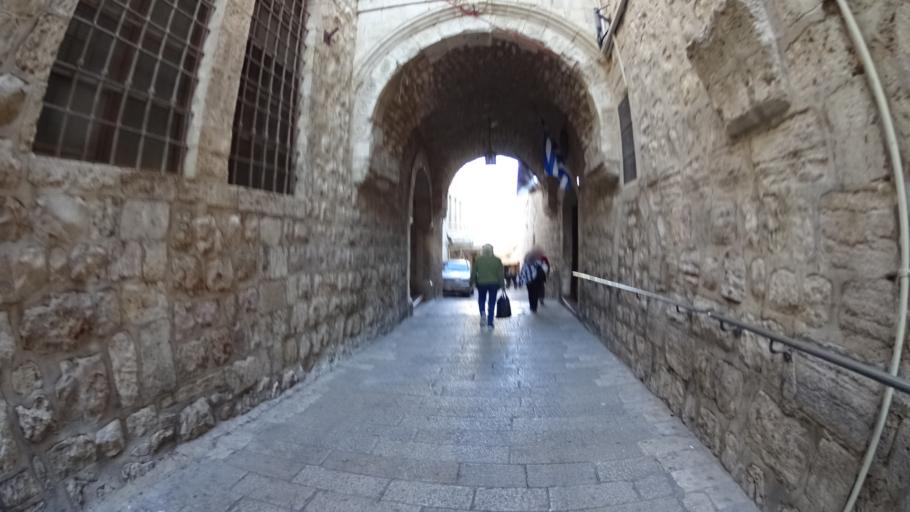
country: PS
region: West Bank
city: Old City
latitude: 31.7786
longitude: 35.2288
